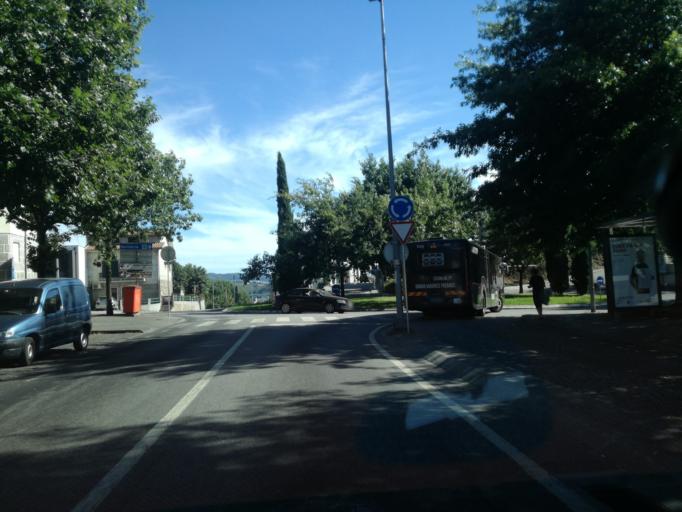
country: PT
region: Braga
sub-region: Guimaraes
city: Guimaraes
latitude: 41.4561
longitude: -8.2971
